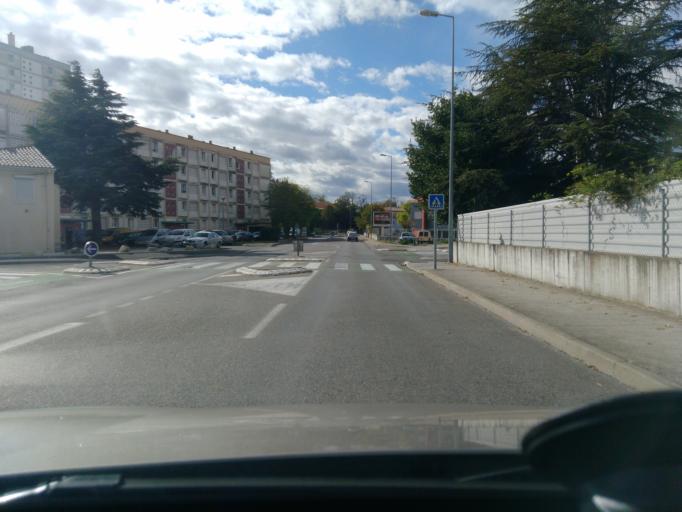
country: FR
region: Rhone-Alpes
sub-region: Departement de la Drome
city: Montelimar
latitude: 44.5557
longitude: 4.7612
